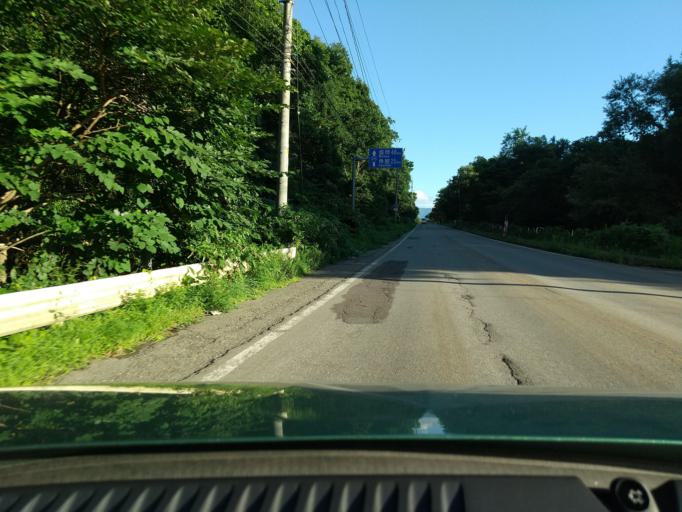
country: JP
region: Akita
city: Kakunodatemachi
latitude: 39.7361
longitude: 140.7180
